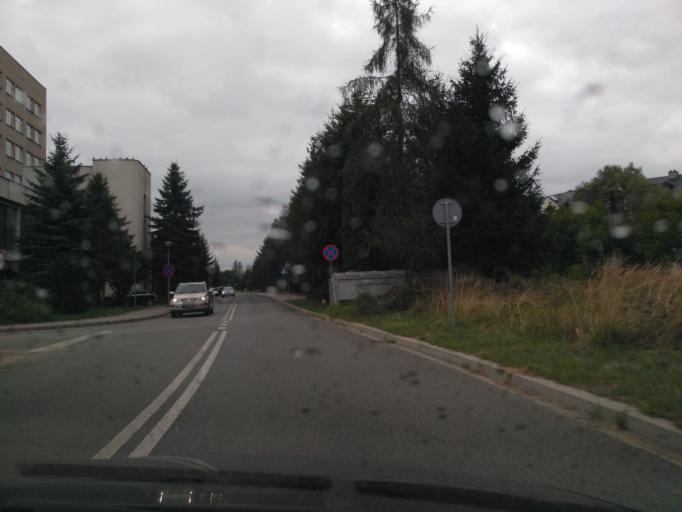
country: PL
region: Subcarpathian Voivodeship
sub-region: Krosno
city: Krosno
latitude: 49.6789
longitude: 21.7771
